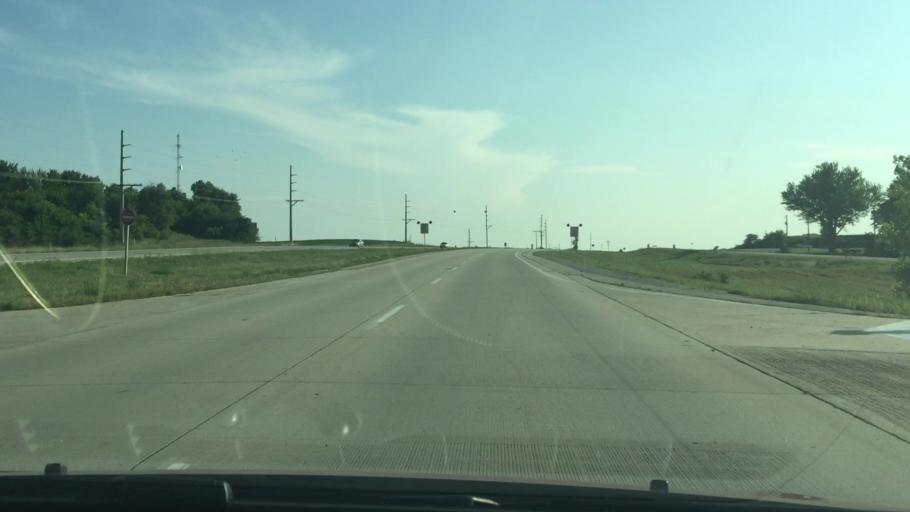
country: US
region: Iowa
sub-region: Muscatine County
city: Muscatine
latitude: 41.4674
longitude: -91.0045
